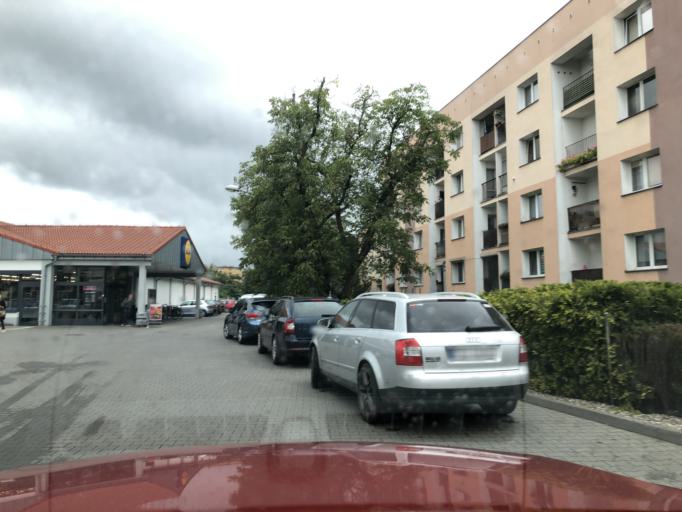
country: PL
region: Greater Poland Voivodeship
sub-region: Powiat szamotulski
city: Wronki
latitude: 52.7091
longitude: 16.3793
